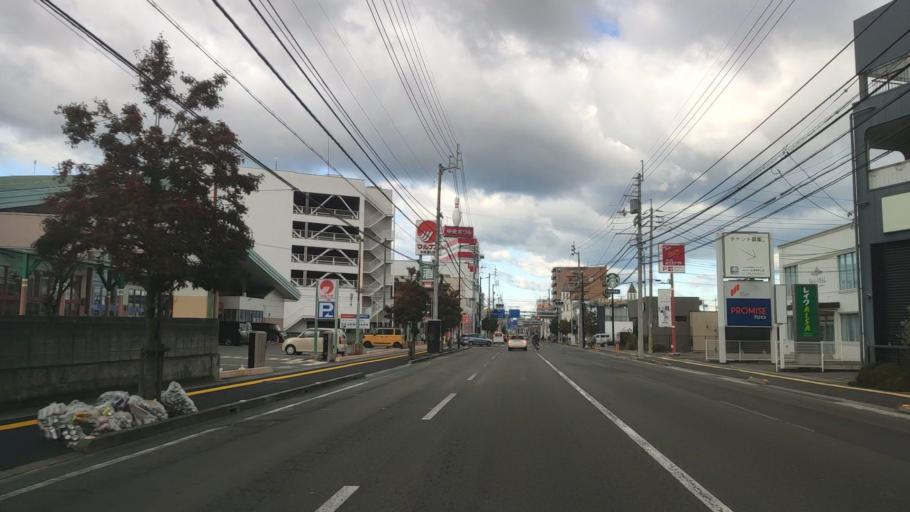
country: JP
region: Ehime
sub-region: Shikoku-chuo Shi
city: Matsuyama
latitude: 33.8537
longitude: 132.7542
